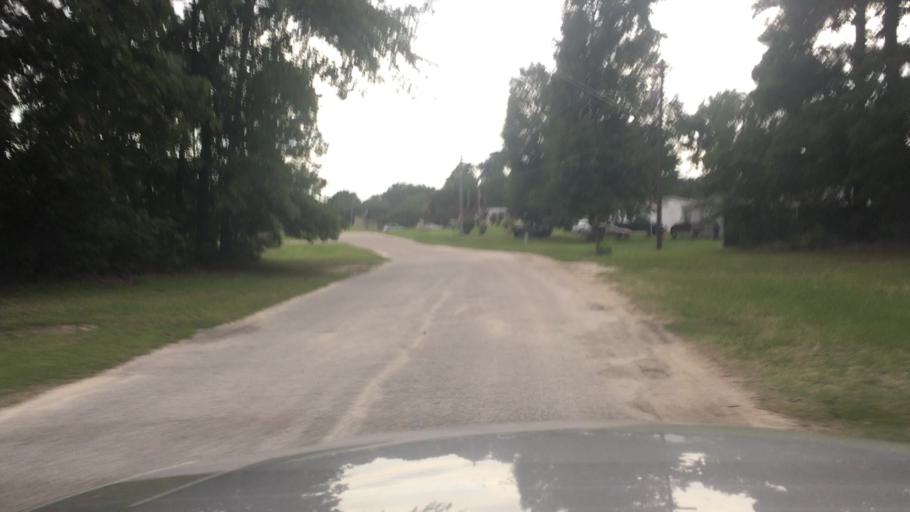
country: US
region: North Carolina
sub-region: Hoke County
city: Rockfish
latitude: 34.9856
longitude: -79.0343
